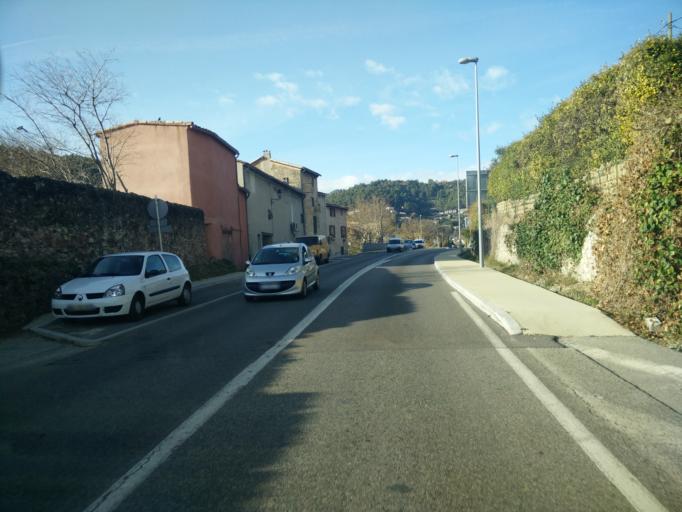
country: FR
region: Provence-Alpes-Cote d'Azur
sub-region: Departement du Var
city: Sollies-Pont
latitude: 43.1986
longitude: 6.0338
